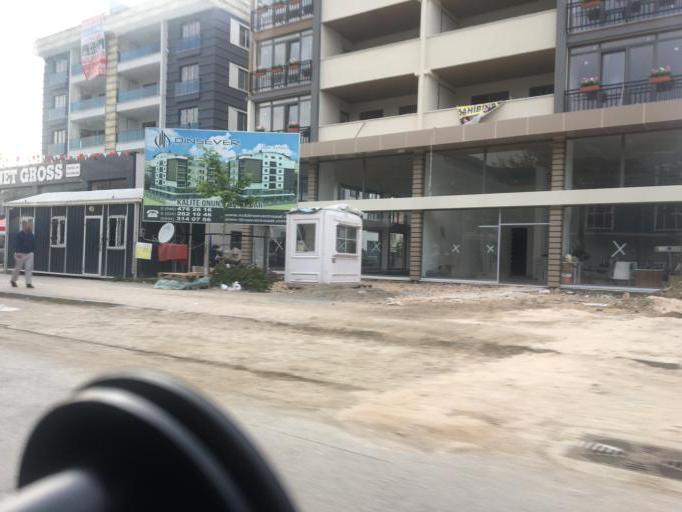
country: TR
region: Bursa
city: Yildirim
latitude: 40.2110
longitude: 29.0390
